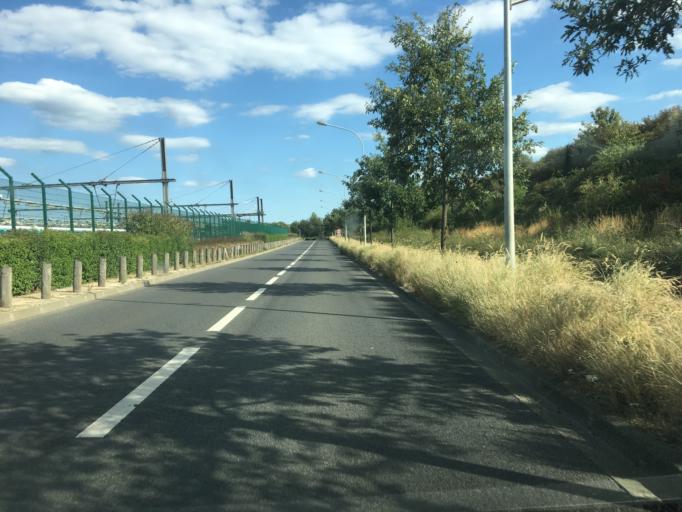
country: FR
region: Ile-de-France
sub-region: Departement du Val-de-Marne
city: Creteil
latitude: 48.7658
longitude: 2.4605
